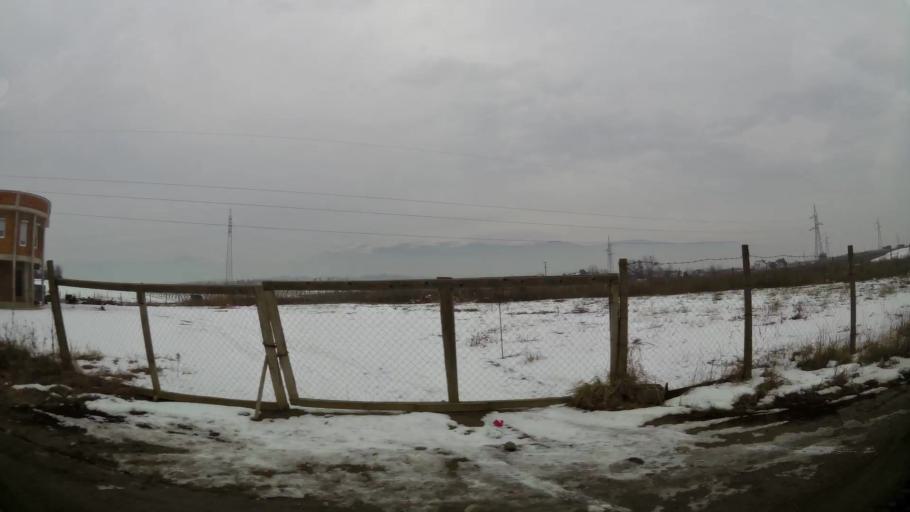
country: MK
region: Suto Orizari
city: Suto Orizare
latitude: 42.0458
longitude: 21.4324
